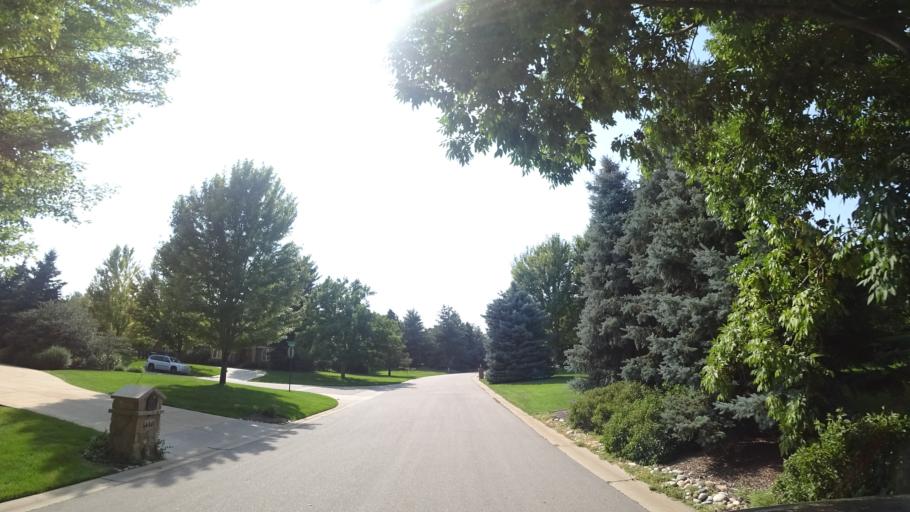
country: US
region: Colorado
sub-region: Arapahoe County
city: Greenwood Village
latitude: 39.6181
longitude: -104.9633
